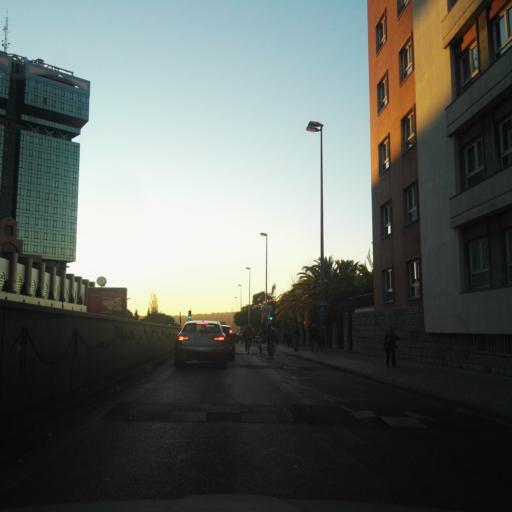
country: PT
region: Lisbon
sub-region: Lisbon
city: Lisbon
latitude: 38.7242
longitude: -9.1617
